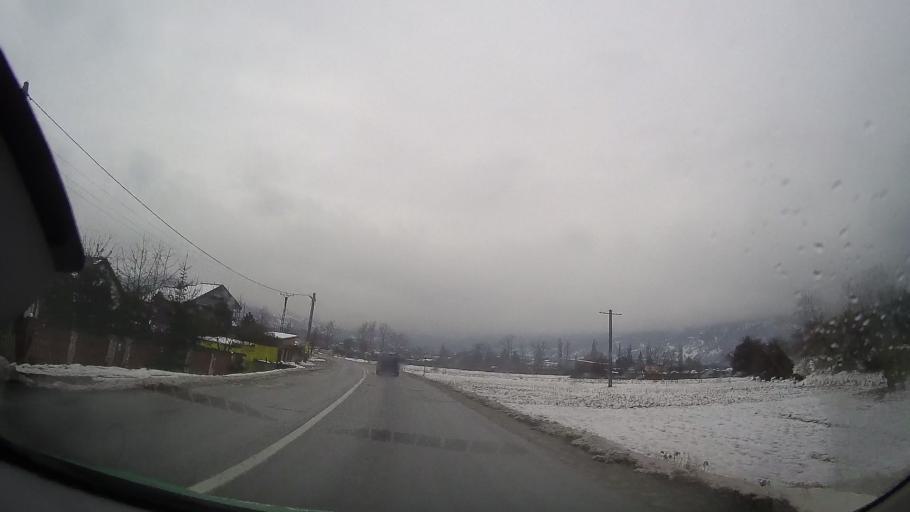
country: RO
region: Neamt
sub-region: Comuna Pangarati
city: Stejaru
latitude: 46.9234
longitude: 26.1900
